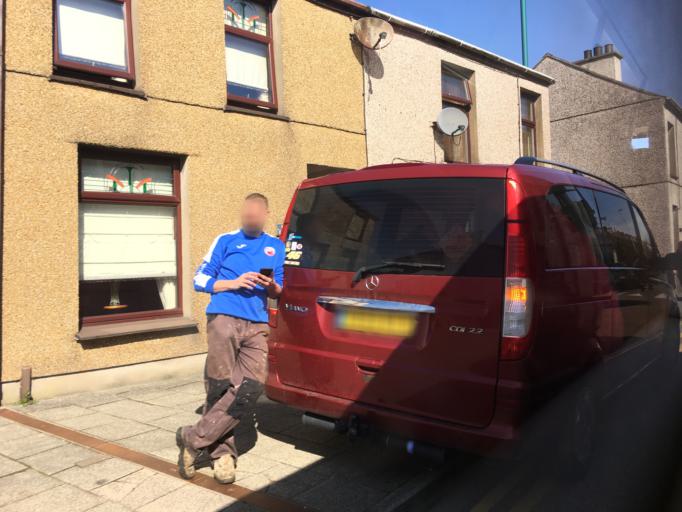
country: GB
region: Wales
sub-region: Gwynedd
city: Llanwnda
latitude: 53.0548
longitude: -4.2836
